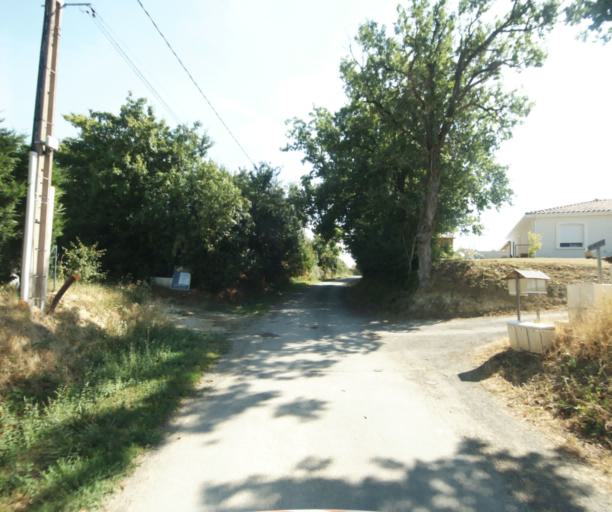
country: FR
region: Midi-Pyrenees
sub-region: Departement de la Haute-Garonne
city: Revel
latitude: 43.4842
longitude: 1.9968
